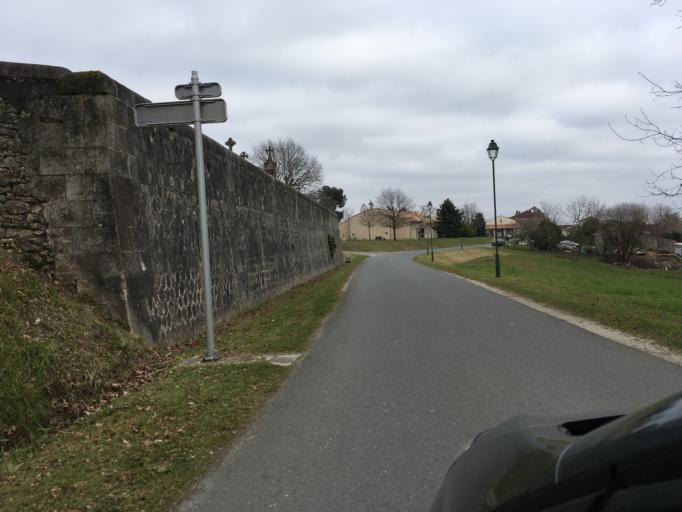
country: FR
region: Aquitaine
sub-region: Departement de la Gironde
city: Saint-Ciers-sur-Gironde
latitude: 45.3143
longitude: -0.5936
